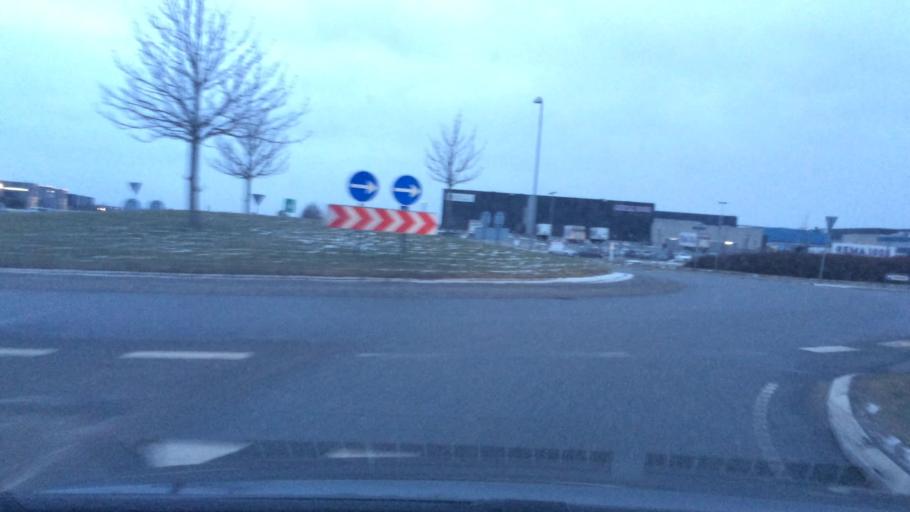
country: DK
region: Central Jutland
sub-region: Horsens Kommune
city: Horsens
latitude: 55.8342
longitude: 9.7987
